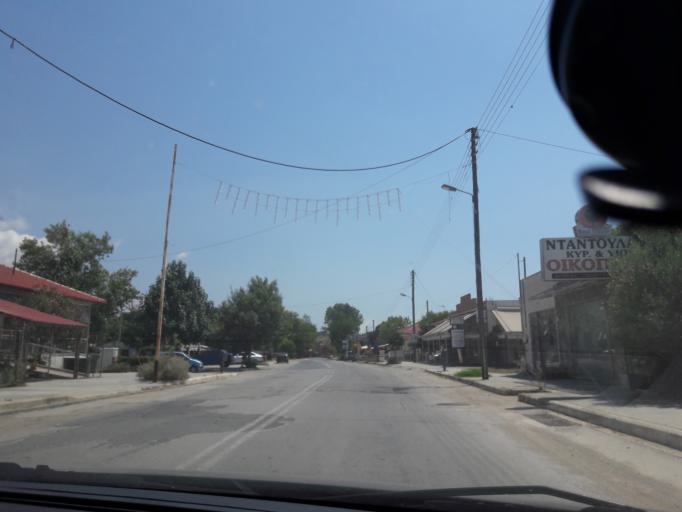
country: GR
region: Central Macedonia
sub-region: Nomos Chalkidikis
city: Nea Kallikrateia
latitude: 40.3393
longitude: 23.0622
